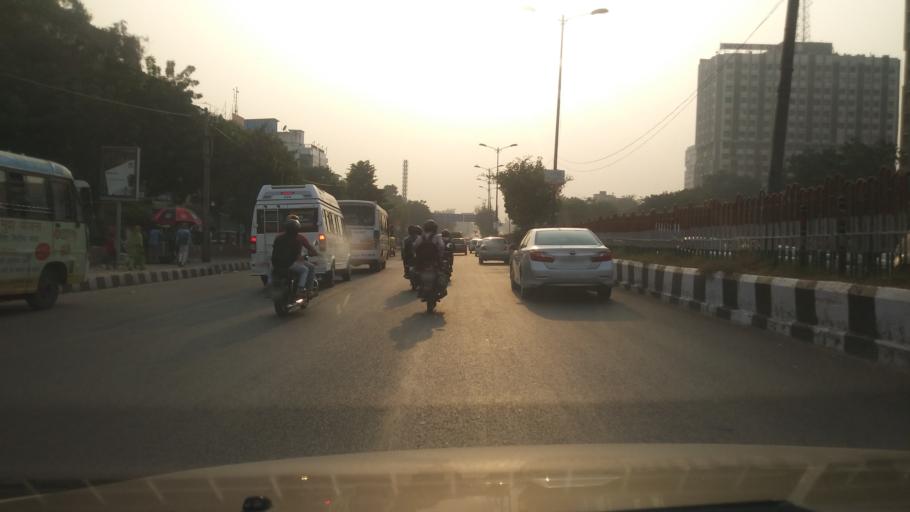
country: IN
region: Uttar Pradesh
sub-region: Gautam Buddha Nagar
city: Noida
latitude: 28.5477
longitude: 77.2545
